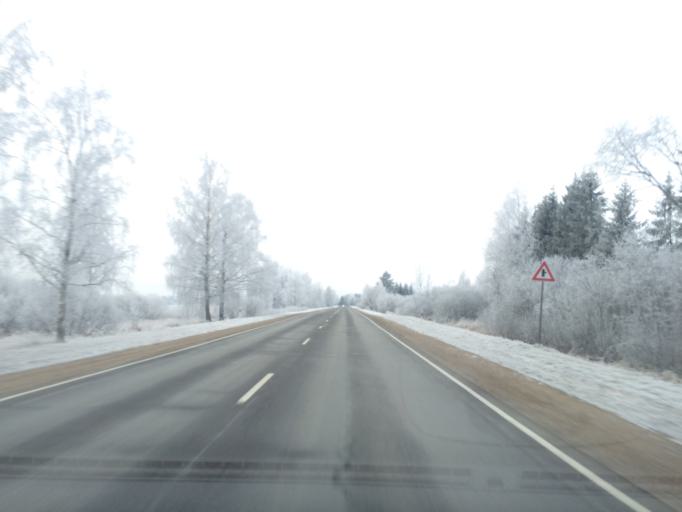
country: LV
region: Rezekne
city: Rezekne
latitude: 56.6358
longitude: 27.4737
